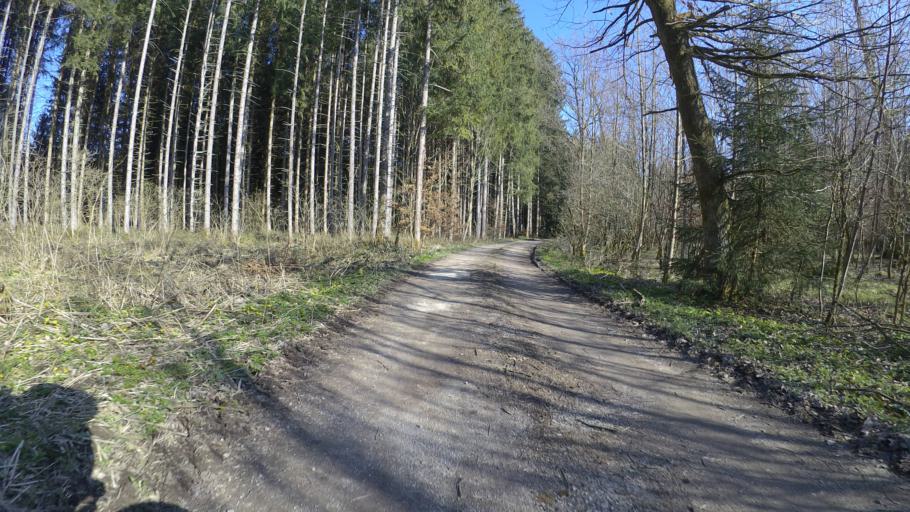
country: DE
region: Bavaria
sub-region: Upper Bavaria
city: Chieming
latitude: 47.8780
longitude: 12.5727
